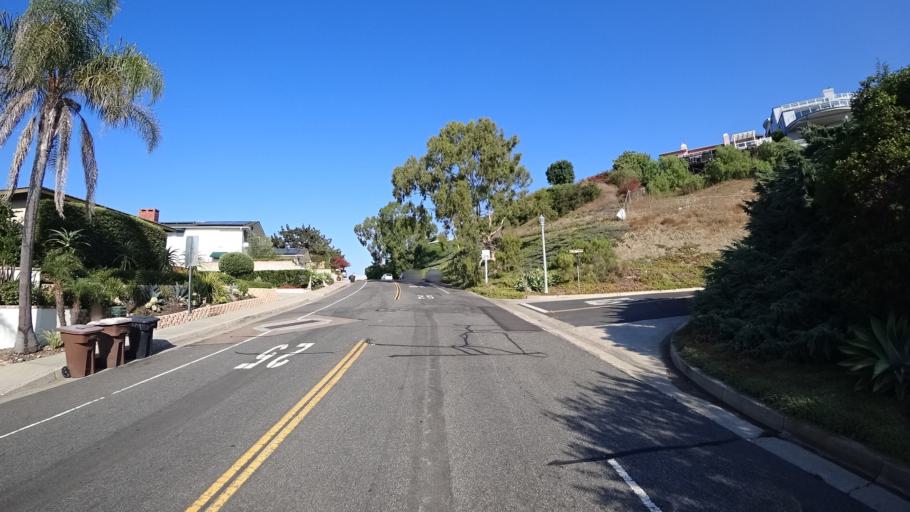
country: US
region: California
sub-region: Orange County
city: San Juan Capistrano
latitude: 33.4664
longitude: -117.6564
